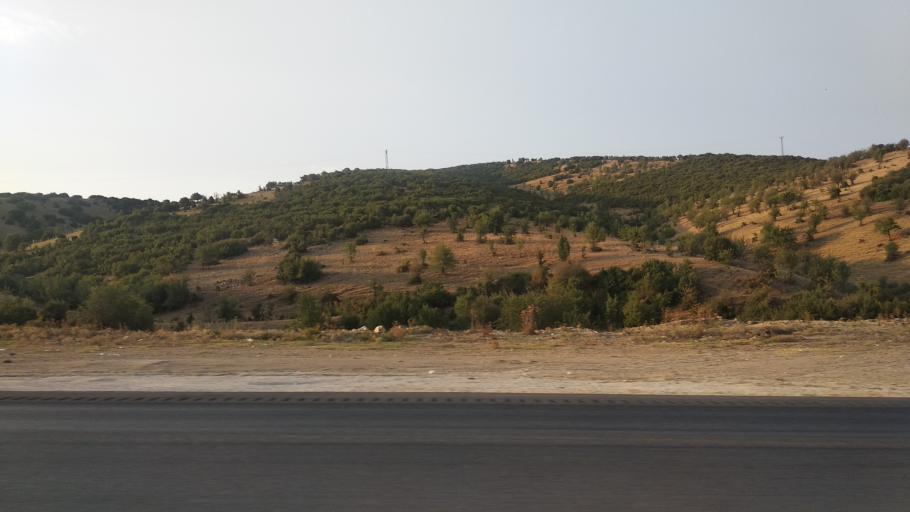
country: TR
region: Manisa
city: Menye
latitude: 38.5541
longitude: 28.4760
